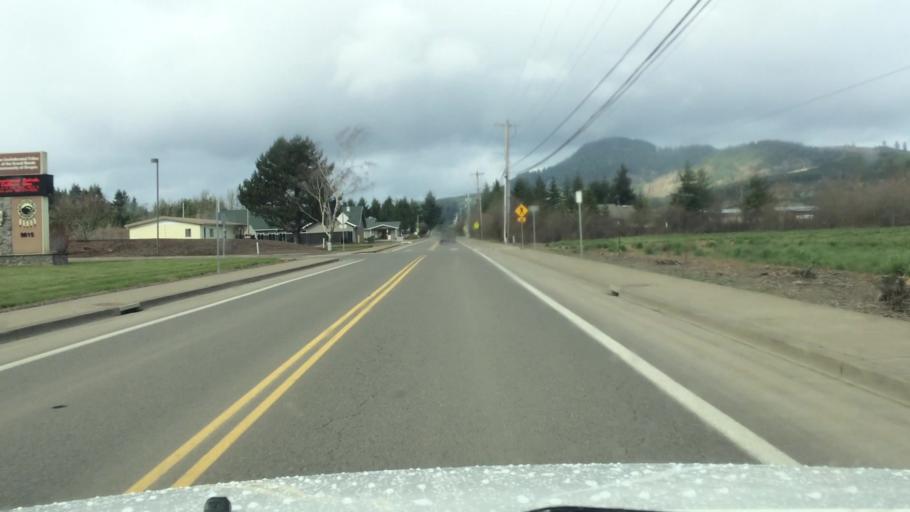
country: US
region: Oregon
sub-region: Polk County
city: Grand Ronde
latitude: 45.0738
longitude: -123.6118
